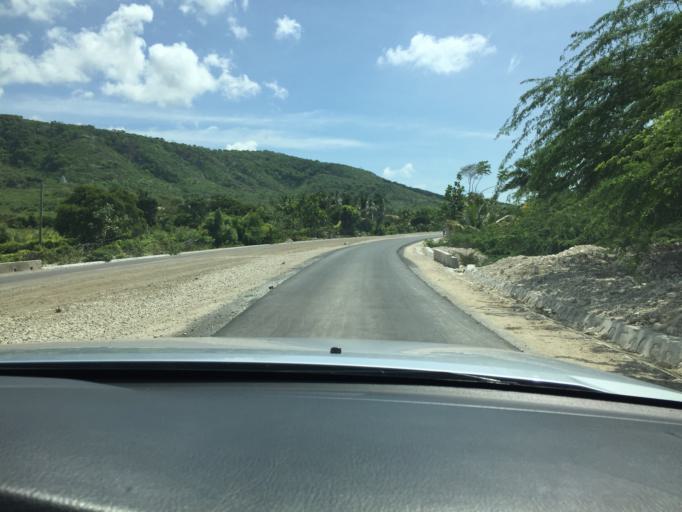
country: HT
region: Sud
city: Aquin
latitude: 18.2530
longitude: -73.3073
